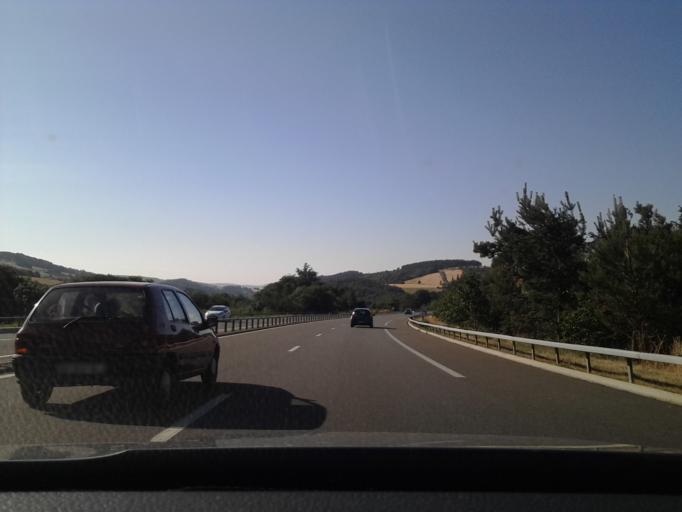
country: FR
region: Languedoc-Roussillon
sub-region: Departement de la Lozere
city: Marvejols
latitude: 44.6194
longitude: 3.2542
